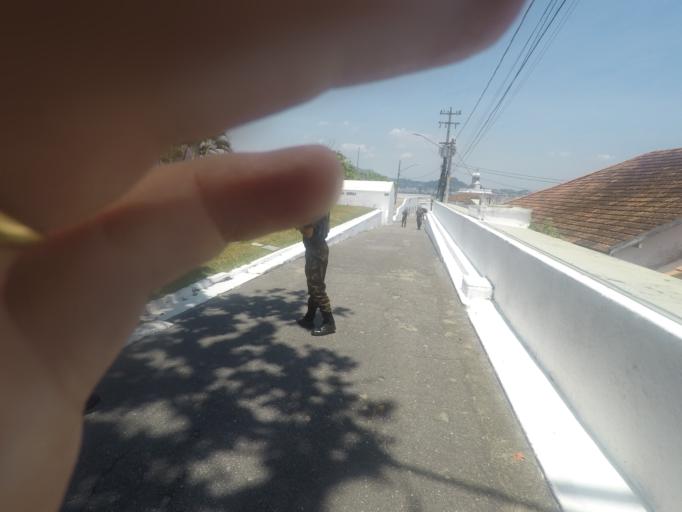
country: BR
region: Rio de Janeiro
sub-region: Niteroi
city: Niteroi
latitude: -22.9383
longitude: -43.1331
